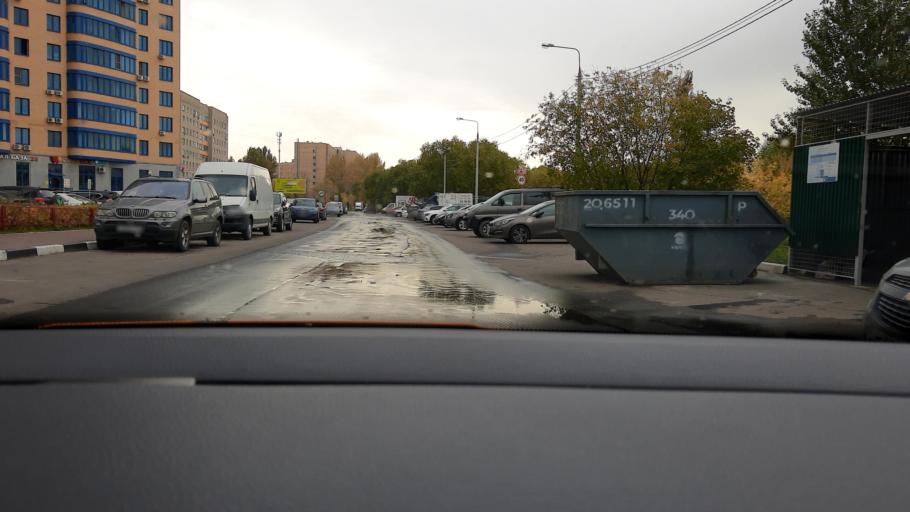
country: RU
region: Moscow
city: Ivanovskoye
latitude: 55.7722
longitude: 37.8461
